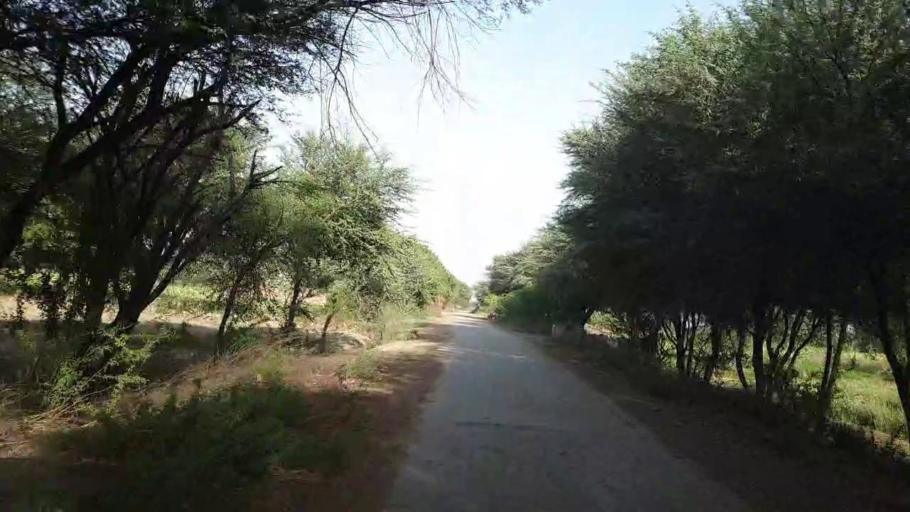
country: PK
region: Sindh
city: Tando Ghulam Ali
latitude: 25.0804
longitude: 68.8978
